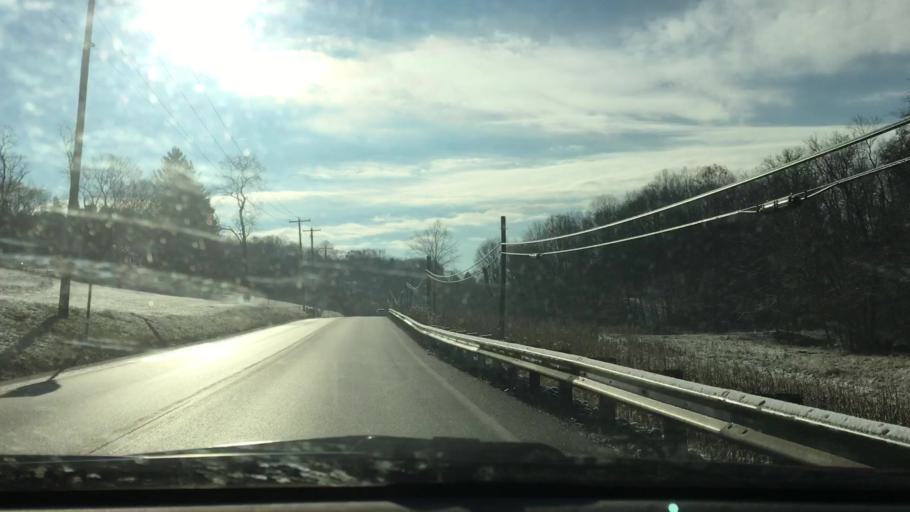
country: US
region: Pennsylvania
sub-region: Allegheny County
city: Oakdale
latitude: 40.4277
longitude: -80.2028
